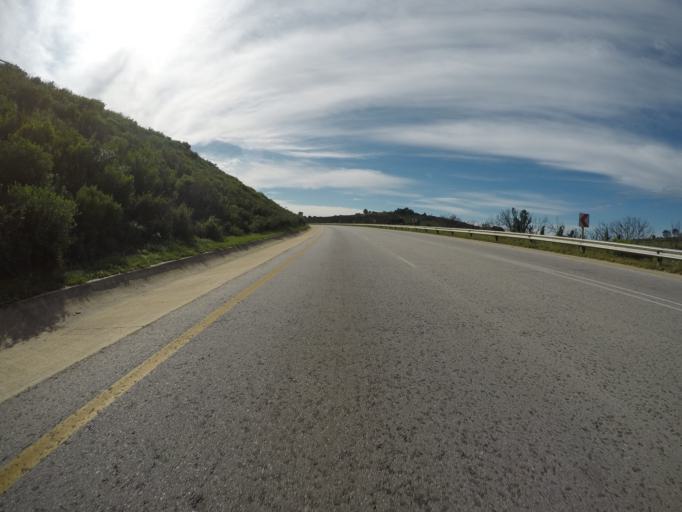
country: ZA
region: Eastern Cape
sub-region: Cacadu District Municipality
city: Jeffrey's Bay
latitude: -33.9030
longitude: 25.1094
